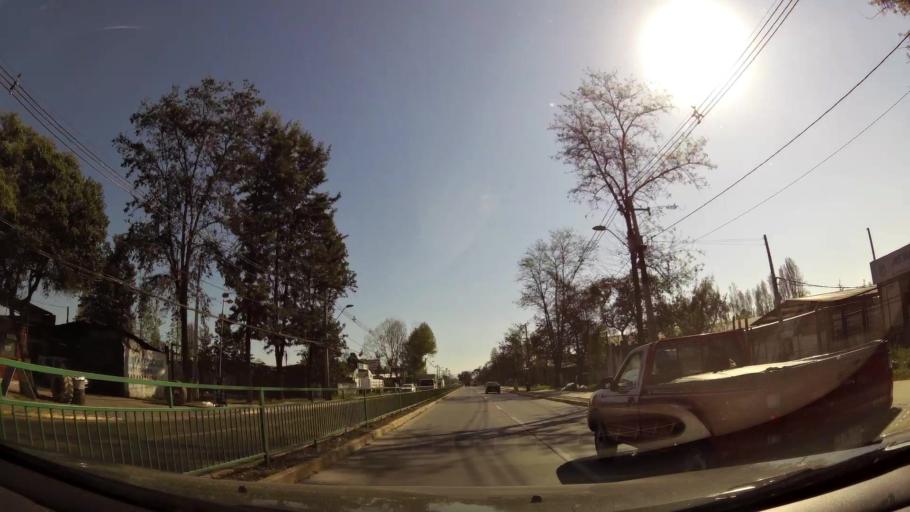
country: CL
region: Santiago Metropolitan
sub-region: Provincia de Santiago
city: La Pintana
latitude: -33.5851
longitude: -70.6245
